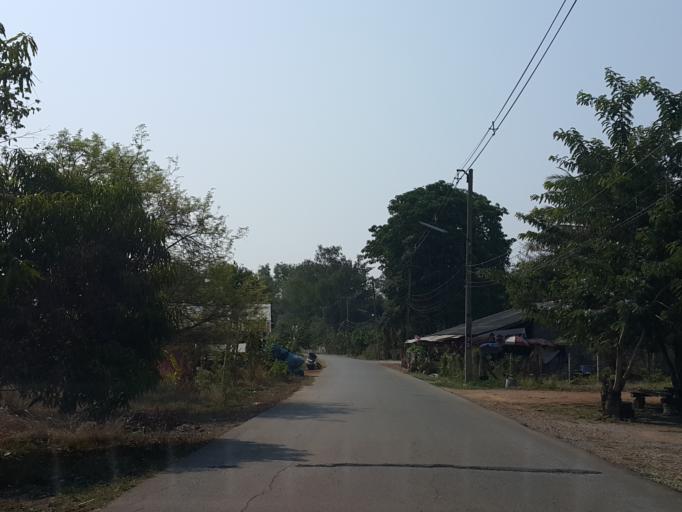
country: TH
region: Kanchanaburi
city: Sai Yok
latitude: 14.1249
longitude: 99.1313
